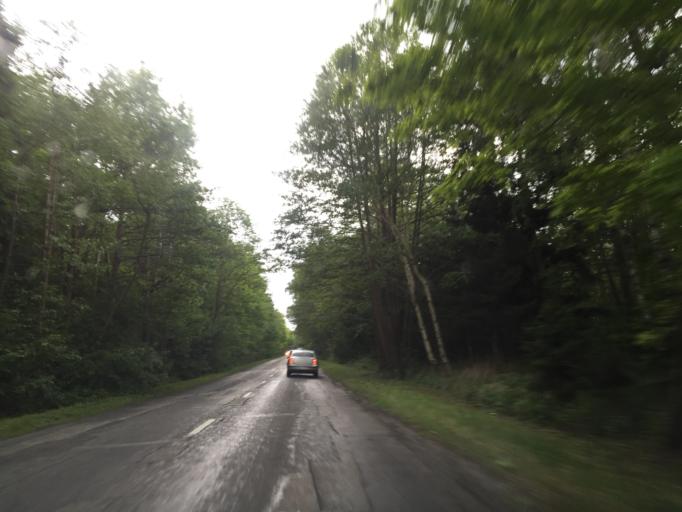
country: LT
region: Klaipedos apskritis
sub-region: Klaipeda
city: Klaipeda
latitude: 55.7411
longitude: 21.0949
